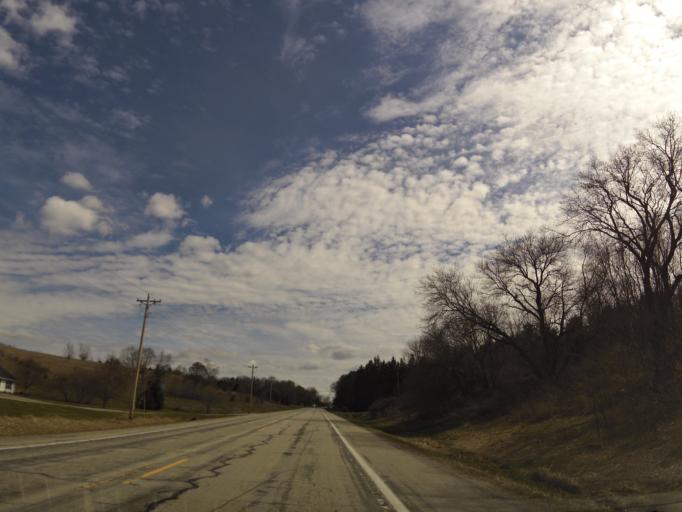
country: US
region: Minnesota
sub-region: Olmsted County
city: Rochester
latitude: 43.9678
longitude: -92.4344
